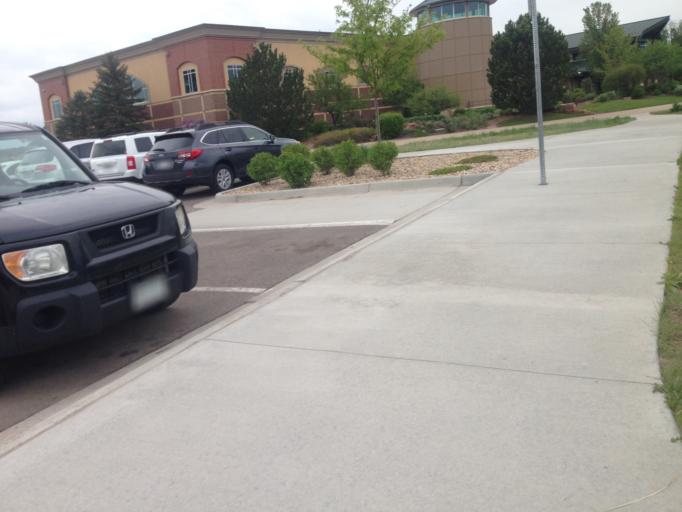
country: US
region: Colorado
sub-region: Boulder County
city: Longmont
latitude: 40.1470
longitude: -105.0976
